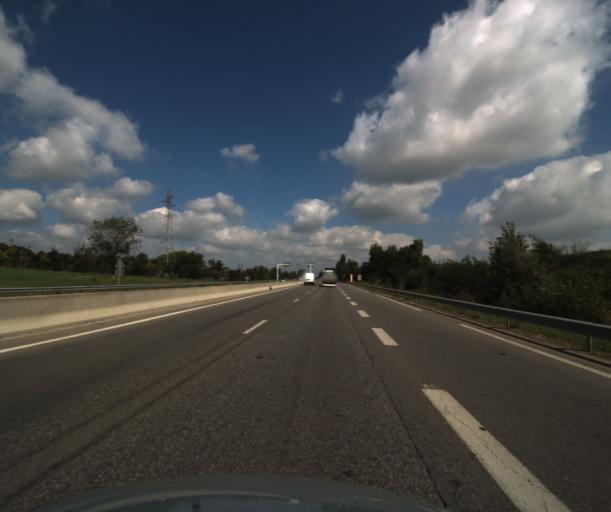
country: FR
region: Midi-Pyrenees
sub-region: Departement de la Haute-Garonne
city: Pinsaguel
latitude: 43.5060
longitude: 1.3849
